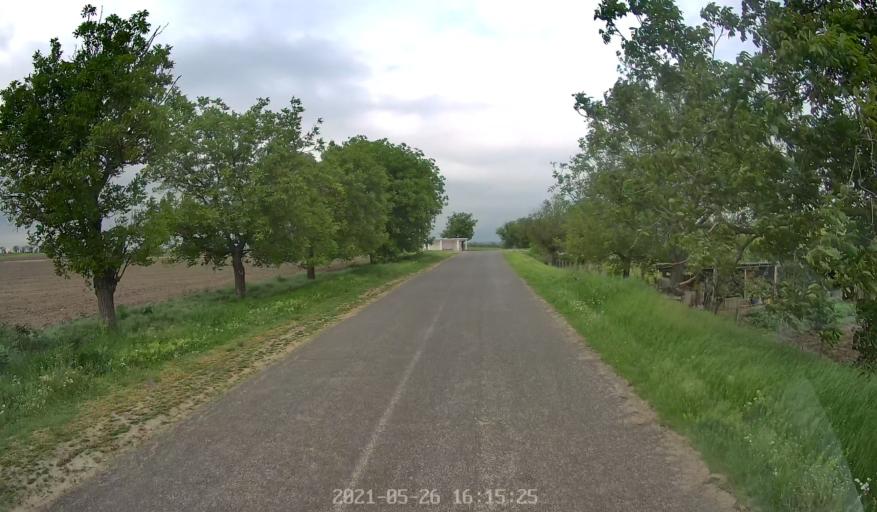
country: MD
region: Hincesti
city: Dancu
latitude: 46.7172
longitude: 28.3470
